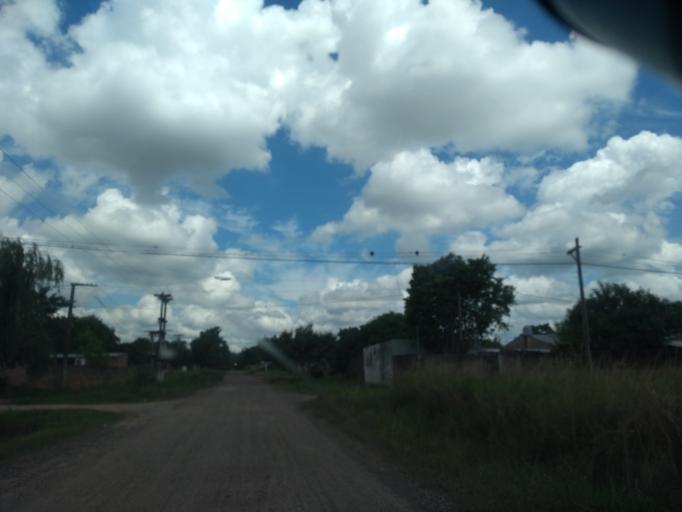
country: AR
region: Chaco
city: Fontana
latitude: -27.4088
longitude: -59.0438
